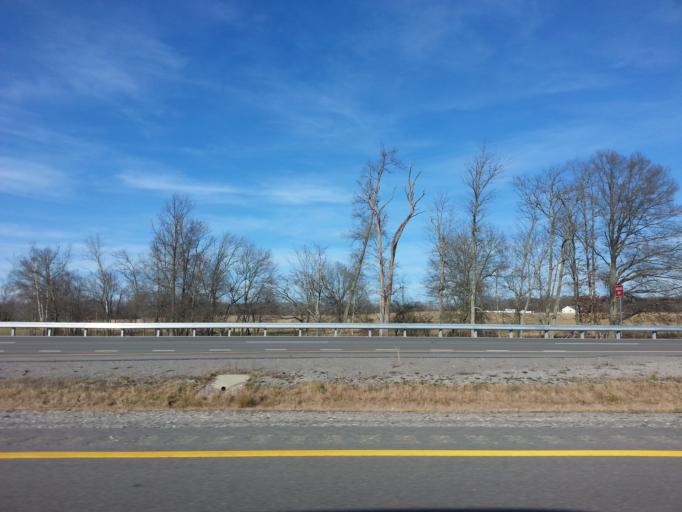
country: US
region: Tennessee
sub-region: Warren County
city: McMinnville
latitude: 35.7134
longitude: -85.8414
